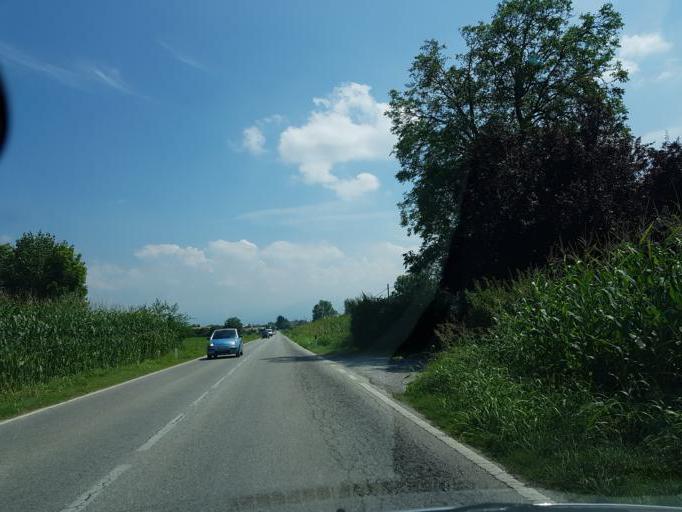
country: IT
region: Piedmont
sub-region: Provincia di Cuneo
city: Caraglio
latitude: 44.4379
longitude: 7.4150
